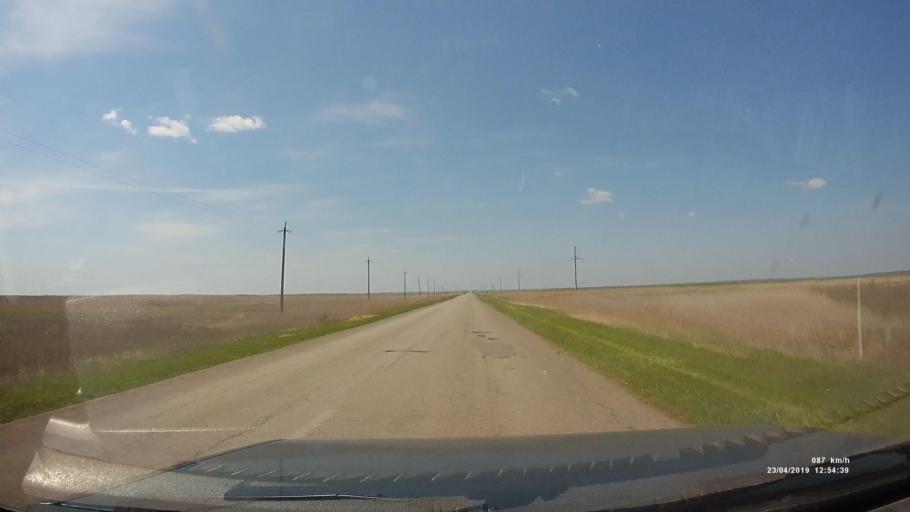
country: RU
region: Kalmykiya
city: Yashalta
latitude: 46.5813
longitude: 42.5751
